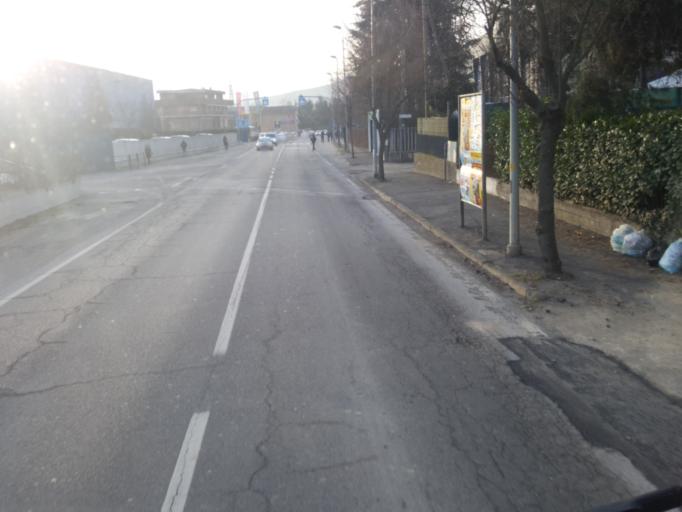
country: IT
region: Piedmont
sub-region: Provincia di Asti
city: Canelli
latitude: 44.7318
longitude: 8.2962
